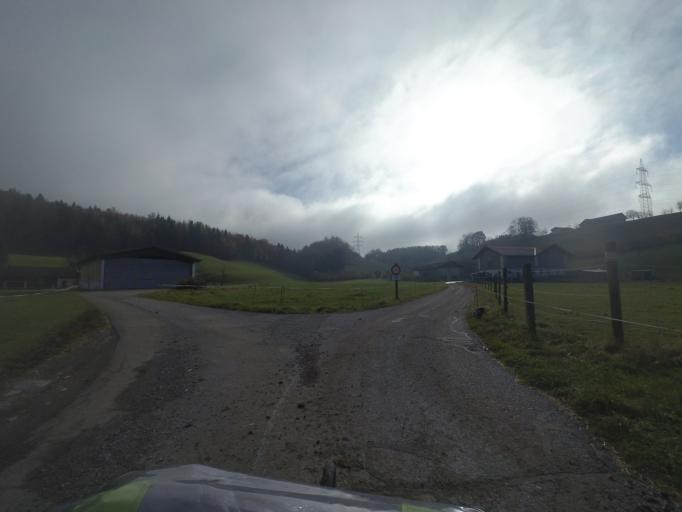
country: AT
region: Salzburg
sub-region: Politischer Bezirk Hallein
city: Adnet
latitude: 47.6789
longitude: 13.1447
